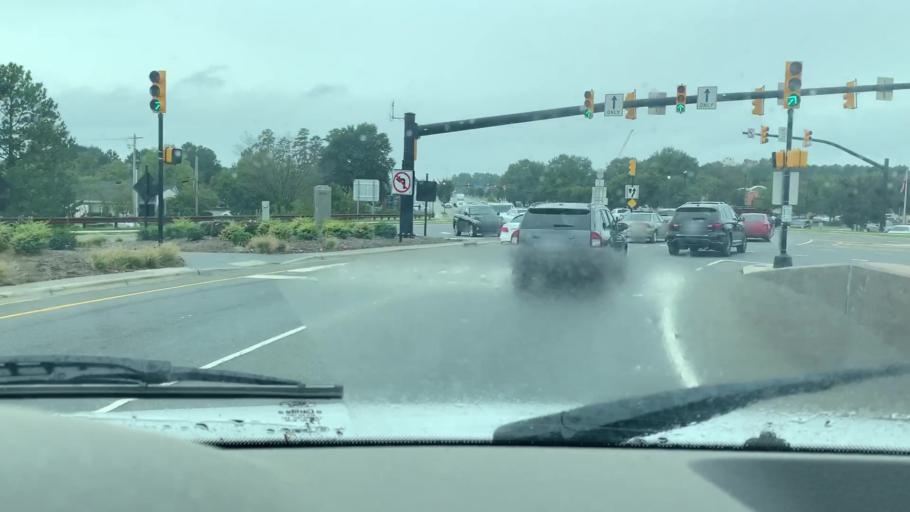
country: US
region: North Carolina
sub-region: Mecklenburg County
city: Cornelius
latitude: 35.4834
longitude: -80.8756
